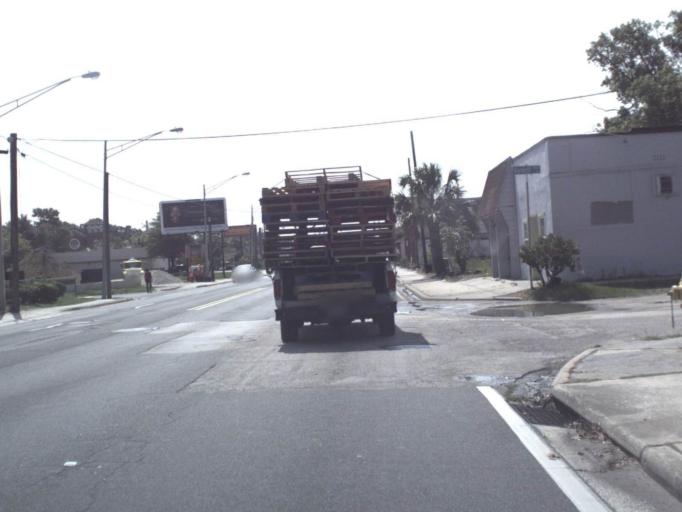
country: US
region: Florida
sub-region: Duval County
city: Jacksonville
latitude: 30.3417
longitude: -81.6780
